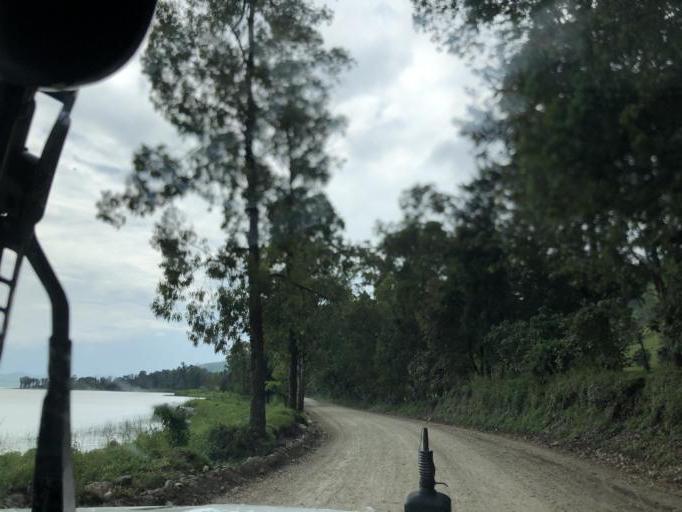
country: CD
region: Nord Kivu
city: Sake
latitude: -1.5974
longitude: 29.0387
